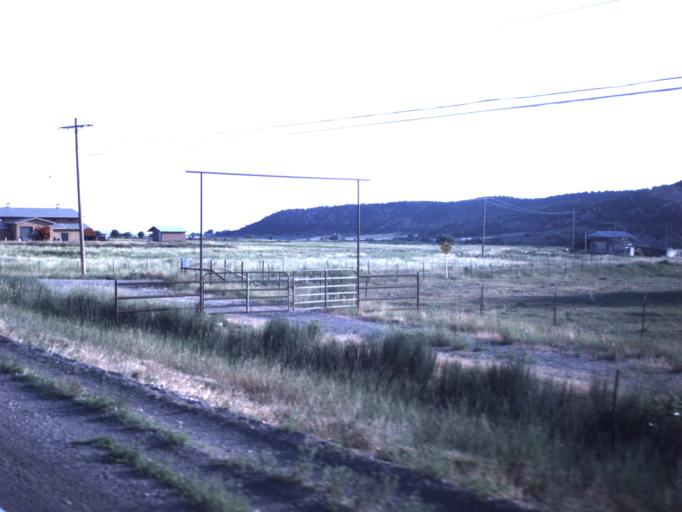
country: US
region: Utah
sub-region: Sanpete County
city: Fairview
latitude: 39.6091
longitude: -111.4448
